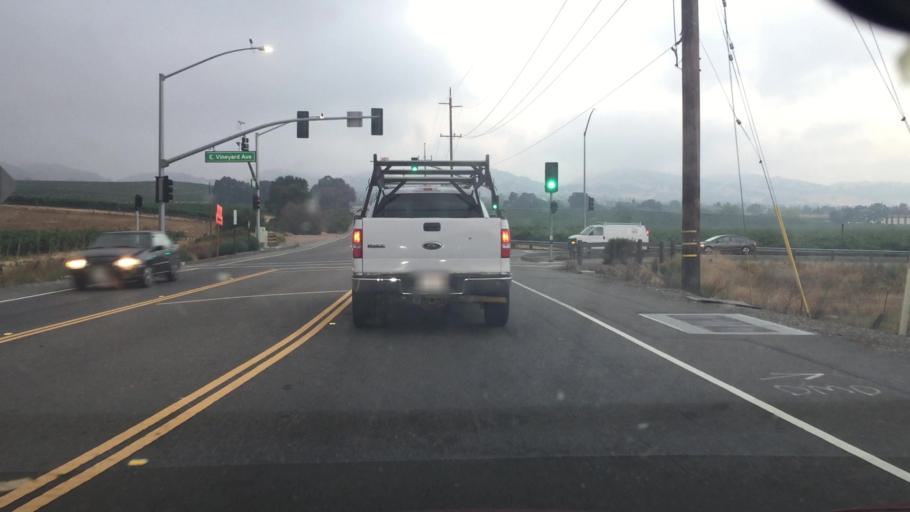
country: US
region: California
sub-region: Alameda County
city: Livermore
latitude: 37.6449
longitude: -121.7889
